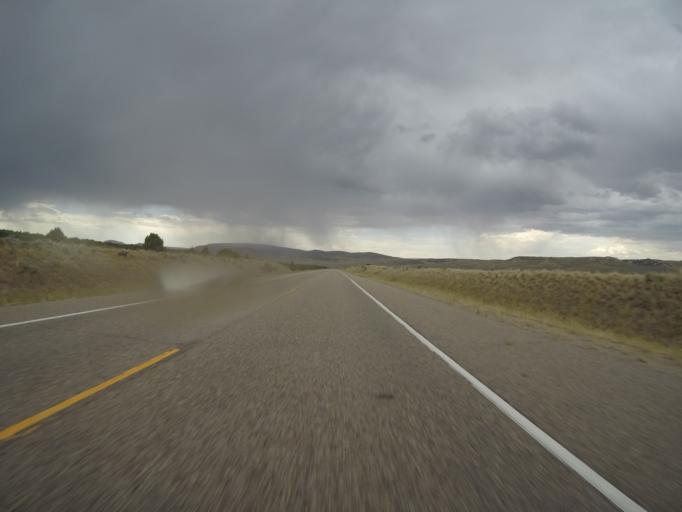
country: US
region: Colorado
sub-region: Rio Blanco County
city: Rangely
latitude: 40.3914
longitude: -108.3464
